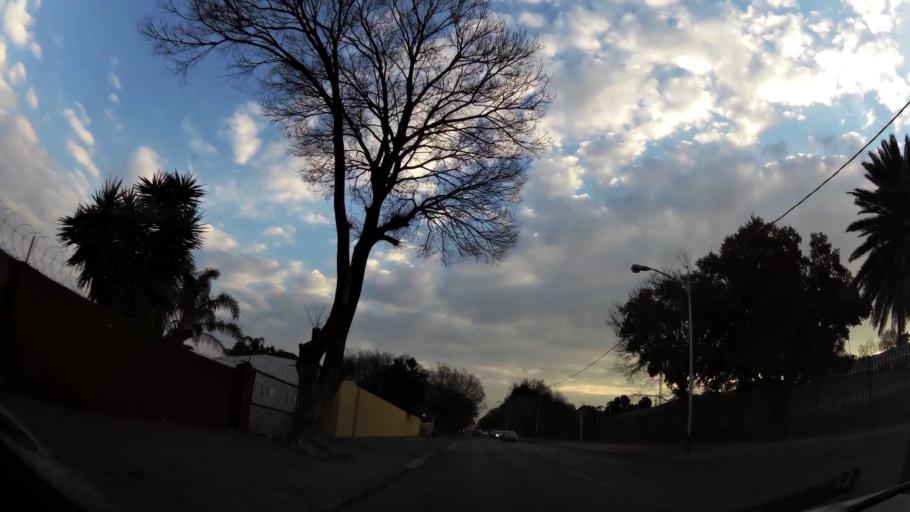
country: ZA
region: Gauteng
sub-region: Ekurhuleni Metropolitan Municipality
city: Germiston
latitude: -26.1862
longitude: 28.1547
